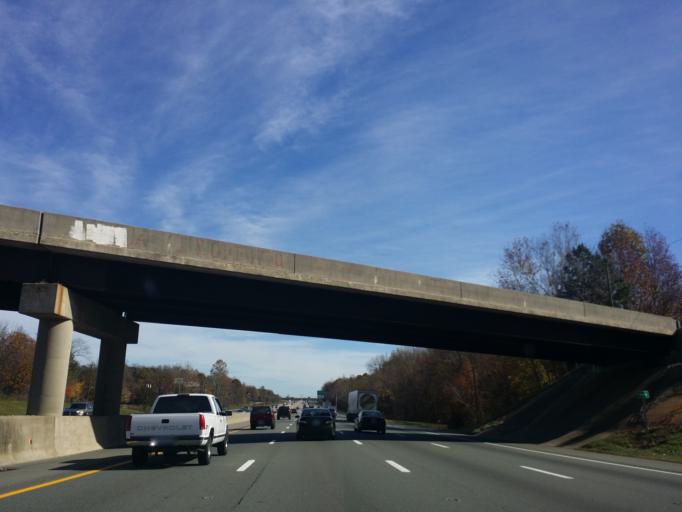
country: US
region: North Carolina
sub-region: Alamance County
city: Mebane
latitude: 36.0777
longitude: -79.2442
